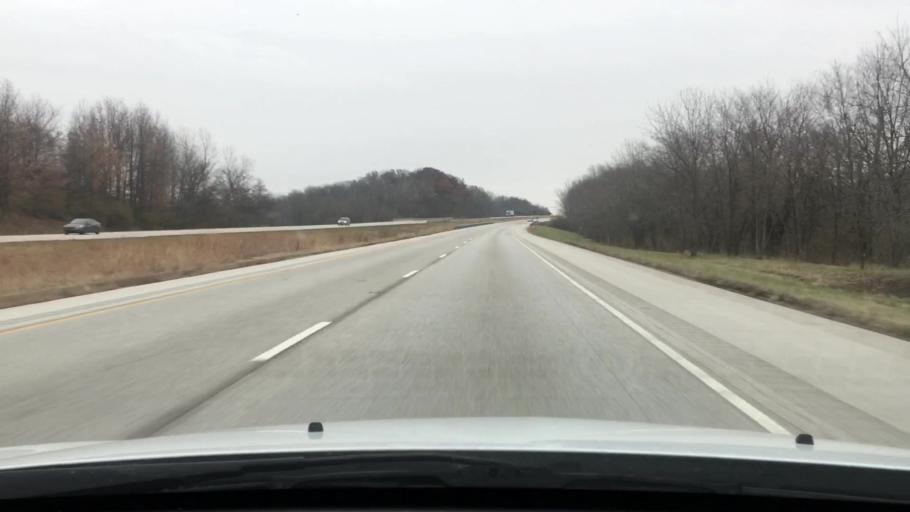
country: US
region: Illinois
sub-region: Scott County
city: Winchester
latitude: 39.6812
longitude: -90.3982
